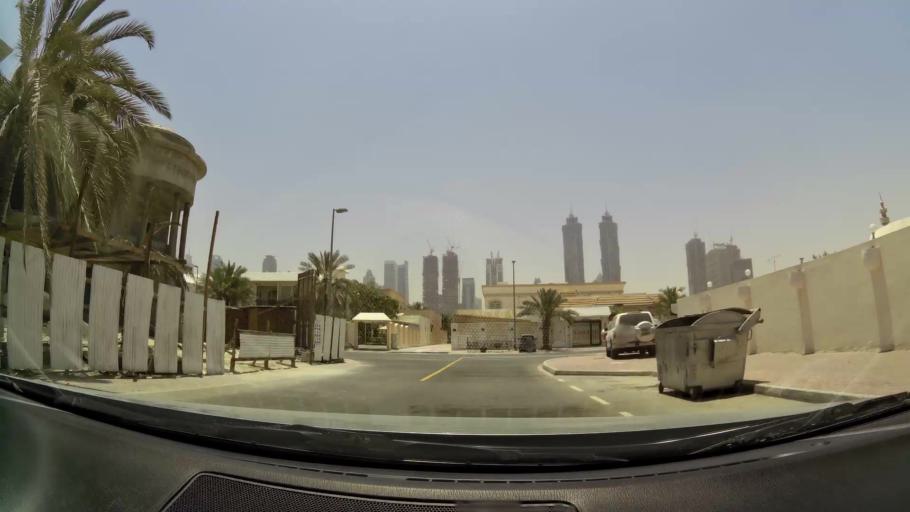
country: AE
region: Dubai
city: Dubai
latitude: 25.1931
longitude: 55.2500
